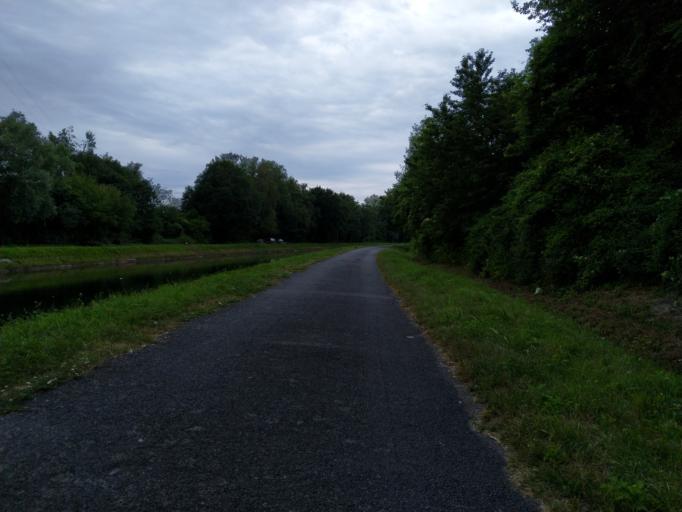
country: BE
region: Wallonia
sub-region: Province du Hainaut
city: Roeulx
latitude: 50.4677
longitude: 4.0810
